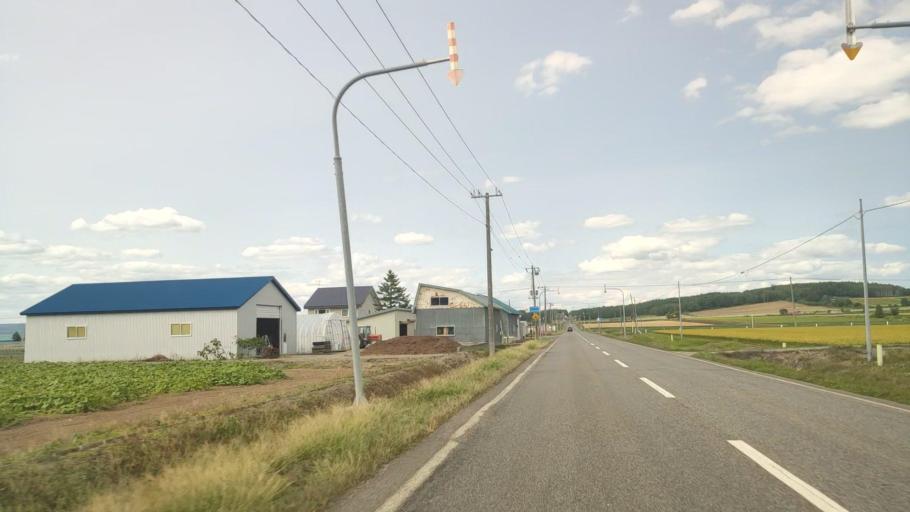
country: JP
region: Hokkaido
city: Nayoro
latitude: 44.2298
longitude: 142.4157
